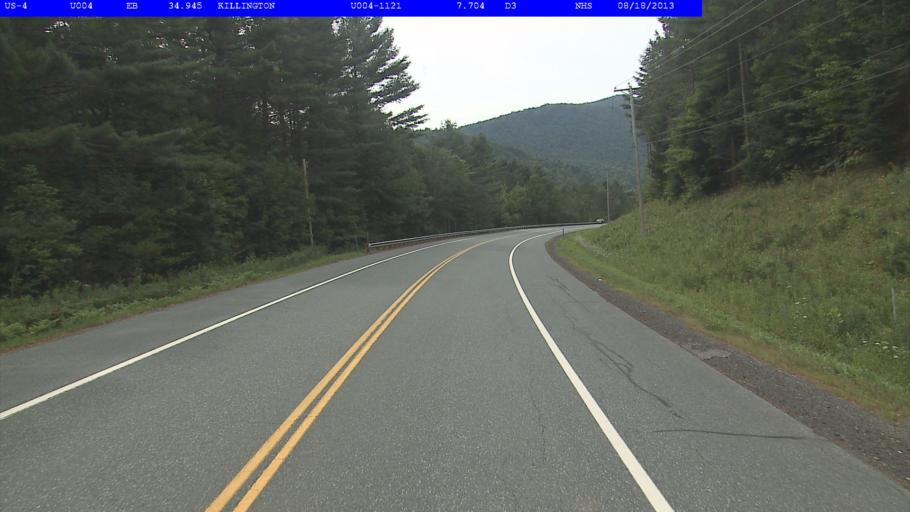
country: US
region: Vermont
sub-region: Rutland County
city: Rutland
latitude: 43.6116
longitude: -72.7522
